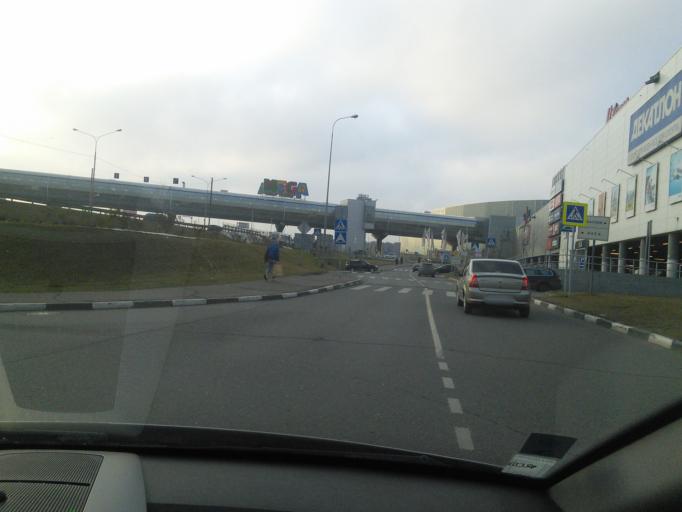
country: RU
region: Moskovskaya
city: Kotel'niki
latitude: 55.6564
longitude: 37.8485
